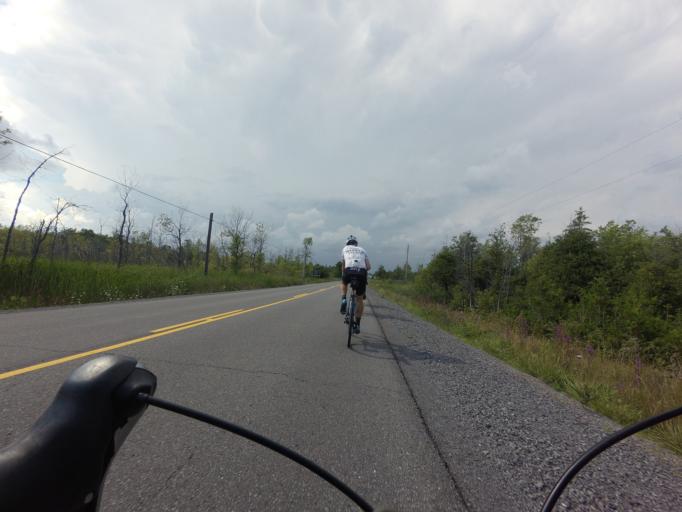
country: CA
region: Ontario
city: Brockville
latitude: 44.7940
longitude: -75.7839
